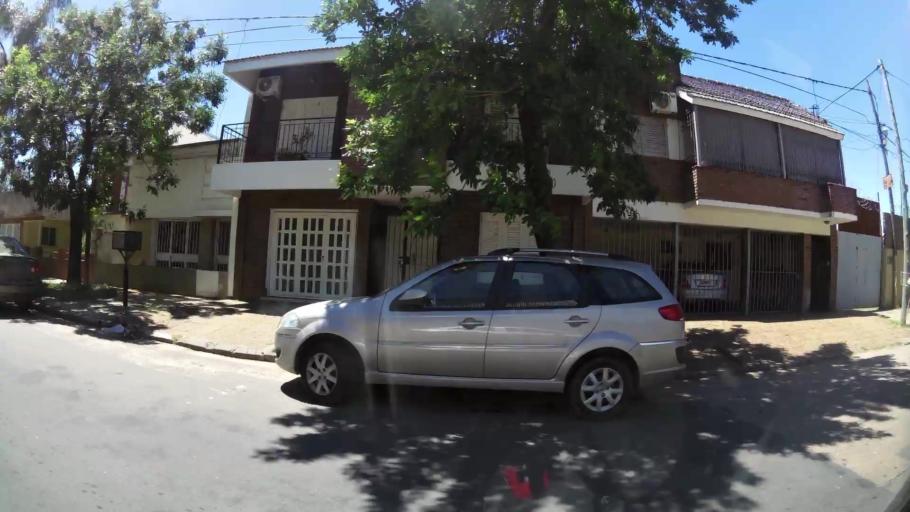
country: AR
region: Santa Fe
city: Santa Fe de la Vera Cruz
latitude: -31.6310
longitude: -60.7075
